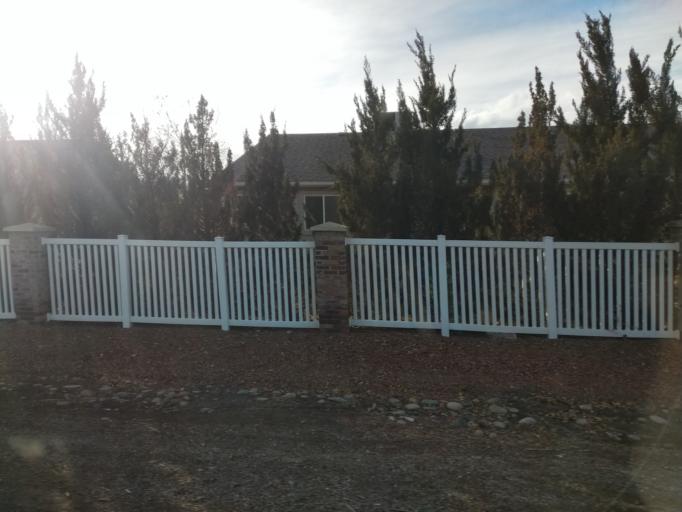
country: US
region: Colorado
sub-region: Mesa County
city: Redlands
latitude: 39.1090
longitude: -108.5896
